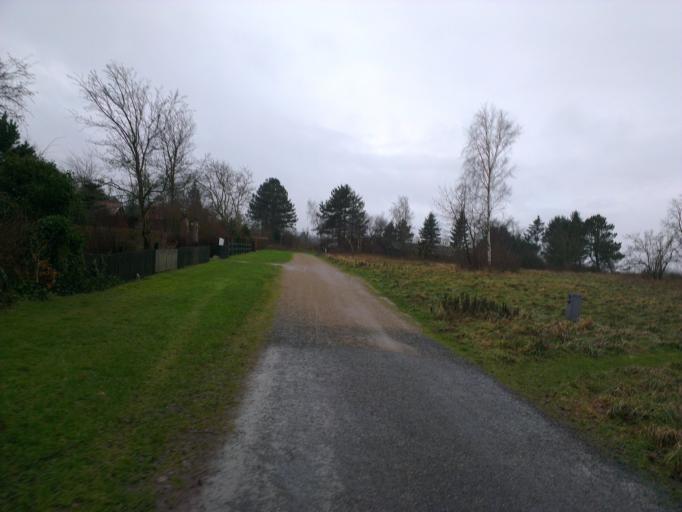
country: DK
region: Capital Region
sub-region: Frederikssund Kommune
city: Jaegerspris
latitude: 55.8377
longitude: 11.9615
